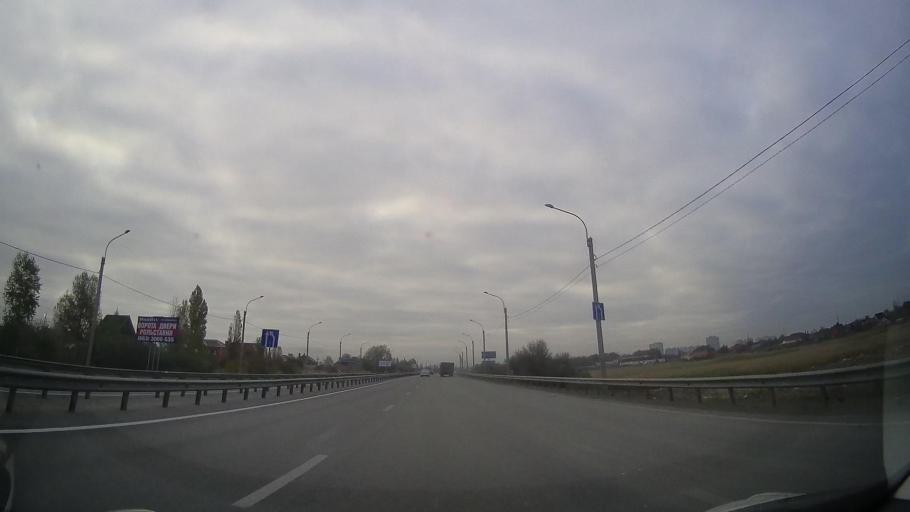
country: RU
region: Rostov
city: Bataysk
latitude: 47.1520
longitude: 39.7718
